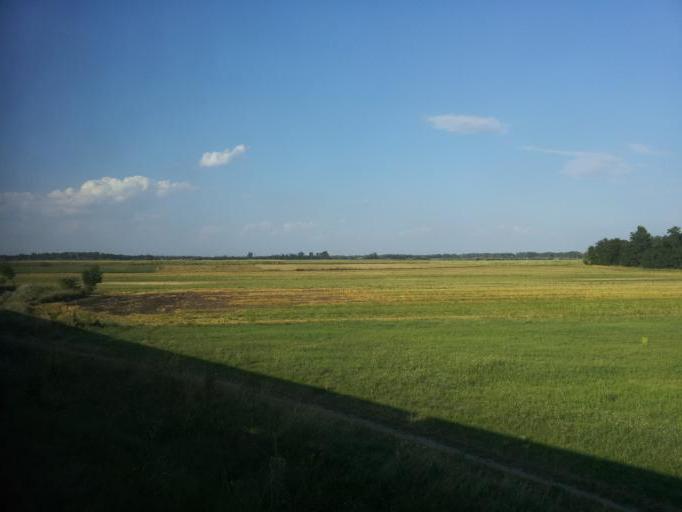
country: HU
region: Pest
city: Dunavarsany
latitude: 47.2893
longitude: 19.0685
